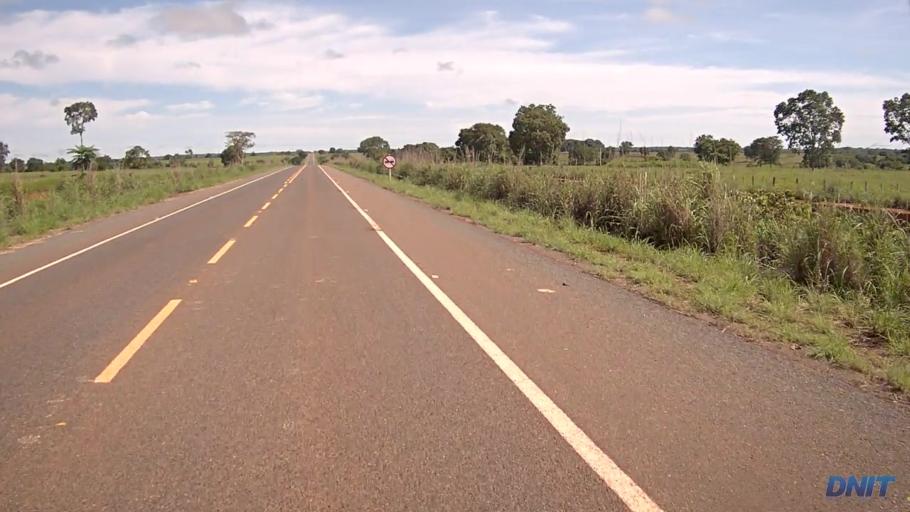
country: BR
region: Goias
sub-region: Sao Miguel Do Araguaia
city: Sao Miguel do Araguaia
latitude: -13.3863
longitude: -50.1392
